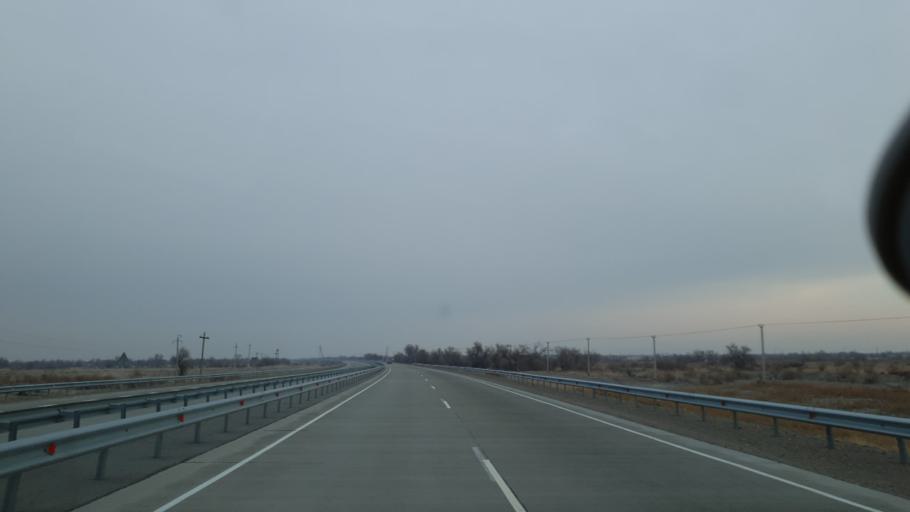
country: KZ
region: Almaty Oblysy
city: Zharkent
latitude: 43.9896
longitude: 79.6423
